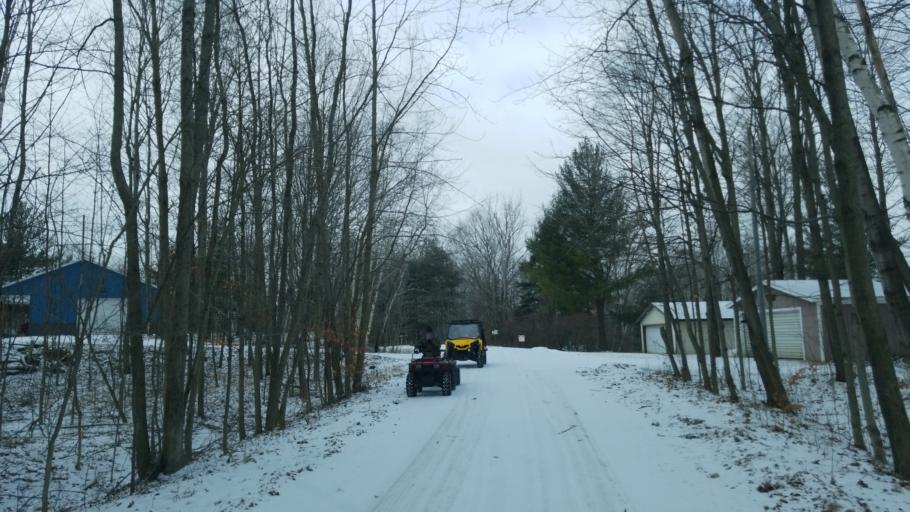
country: US
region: Michigan
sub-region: Osceola County
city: Evart
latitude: 43.8154
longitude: -85.2721
